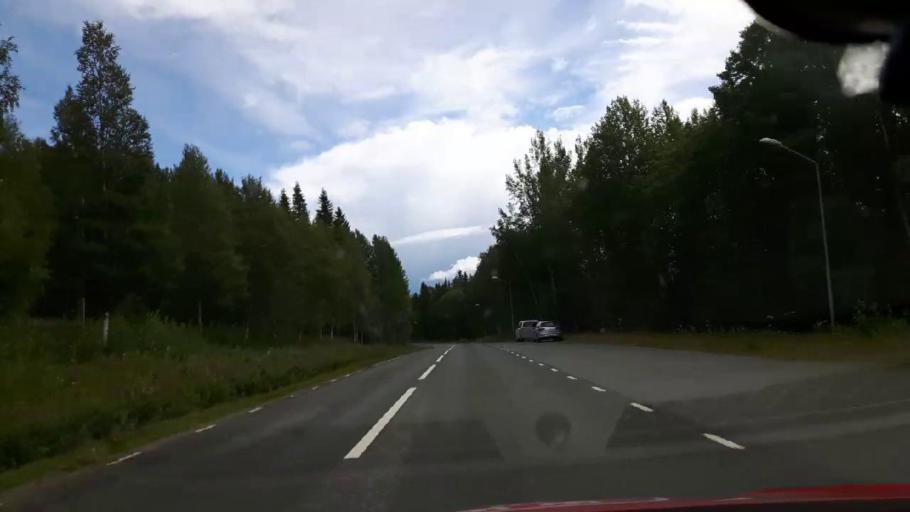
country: SE
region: Jaemtland
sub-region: Stroemsunds Kommun
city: Stroemsund
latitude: 64.3383
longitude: 14.9551
